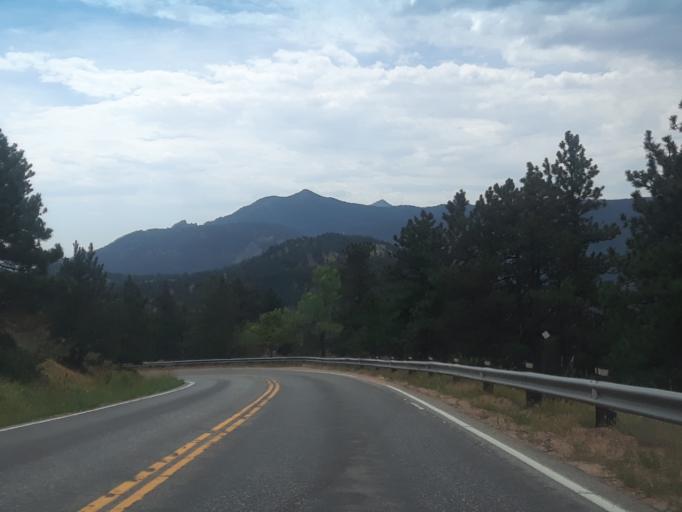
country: US
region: Colorado
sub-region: Boulder County
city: Boulder
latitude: 40.0366
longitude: -105.3270
